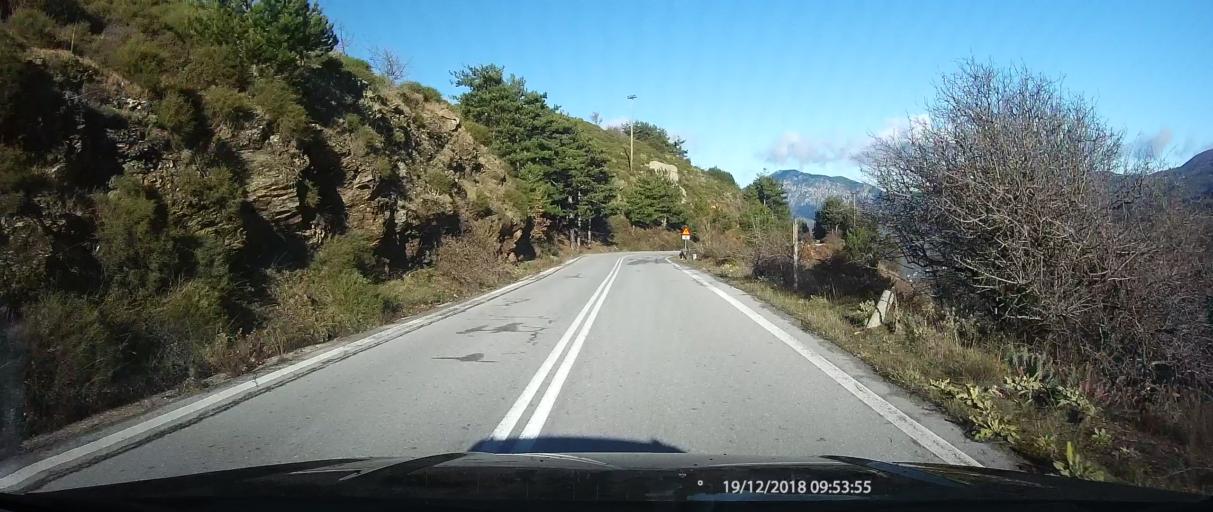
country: GR
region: Peloponnese
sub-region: Nomos Messinias
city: Paralia Vergas
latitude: 37.0771
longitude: 22.2512
